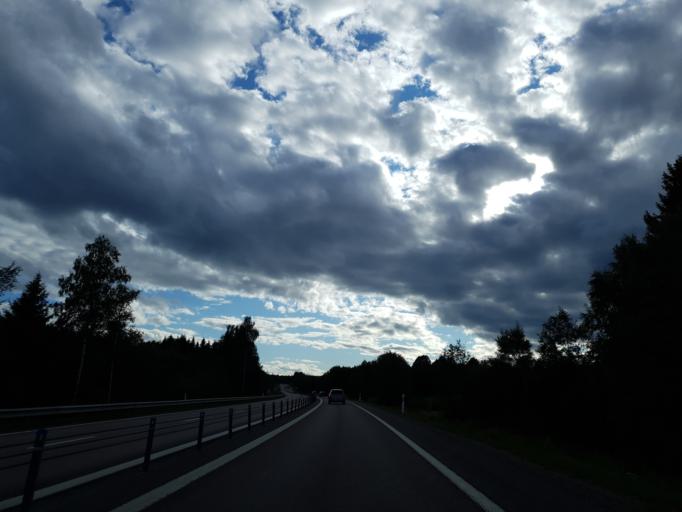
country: SE
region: Vaesternorrland
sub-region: Haernoesands Kommun
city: Haernoesand
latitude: 62.5833
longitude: 17.7709
